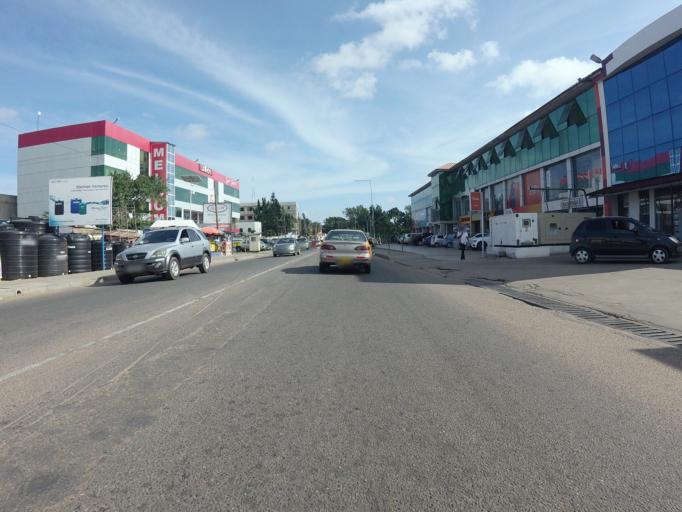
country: GH
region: Greater Accra
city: Medina Estates
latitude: 5.6420
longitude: -0.1622
